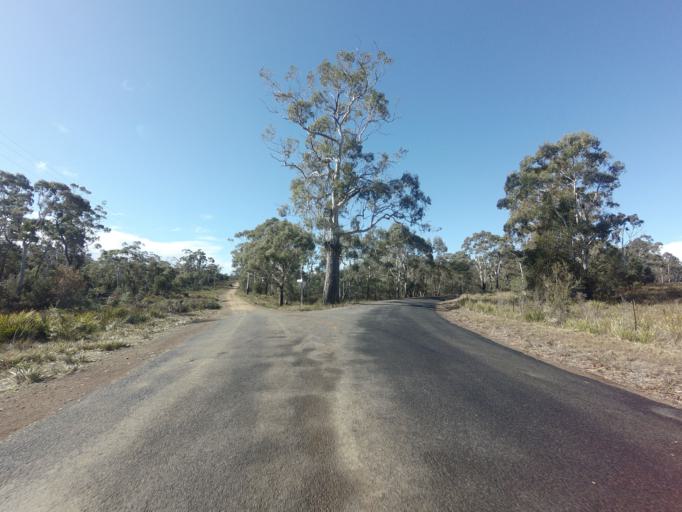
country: AU
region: Tasmania
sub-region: Sorell
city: Sorell
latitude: -42.3574
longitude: 147.9634
